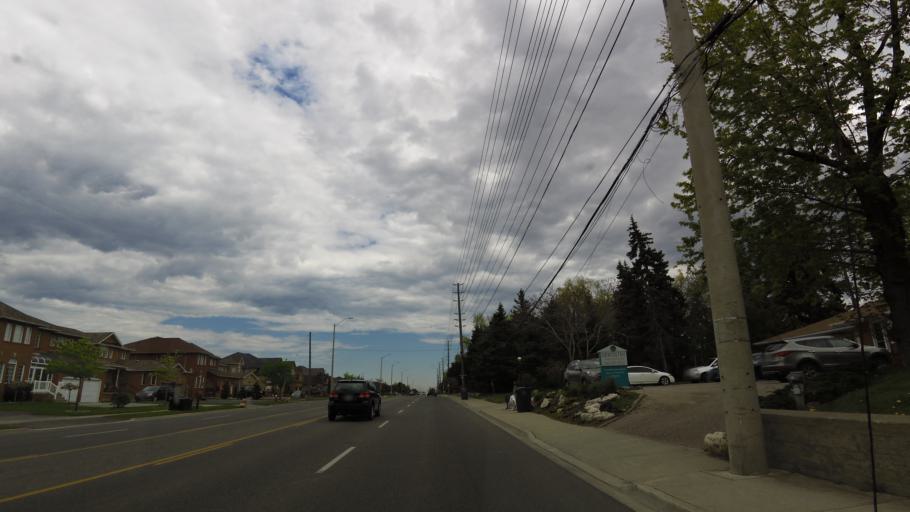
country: CA
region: Ontario
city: Mississauga
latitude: 43.5840
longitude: -79.6935
